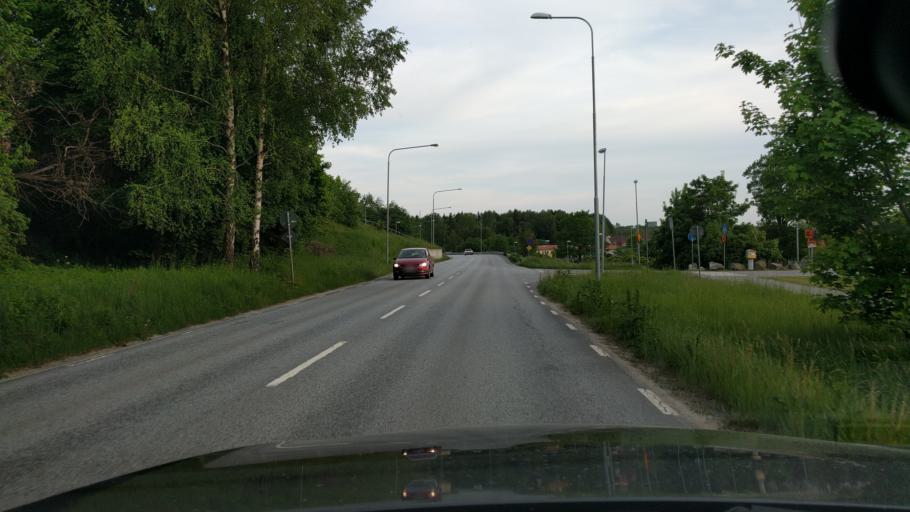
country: SE
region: Stockholm
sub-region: Vallentuna Kommun
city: Vallentuna
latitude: 59.5386
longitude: 18.0907
